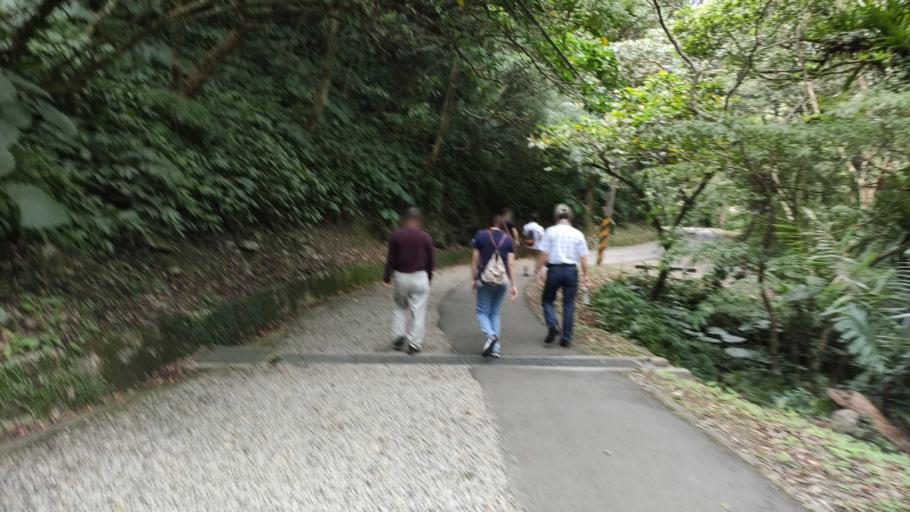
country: TW
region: Taiwan
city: Daxi
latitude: 24.8281
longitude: 121.4462
